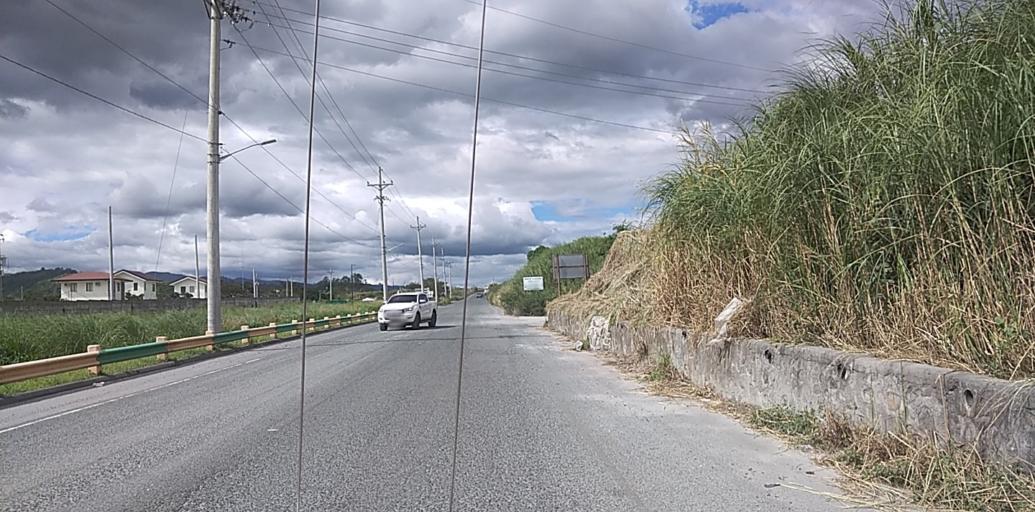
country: PH
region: Central Luzon
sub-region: Province of Pampanga
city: Dolores
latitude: 15.1146
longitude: 120.5155
